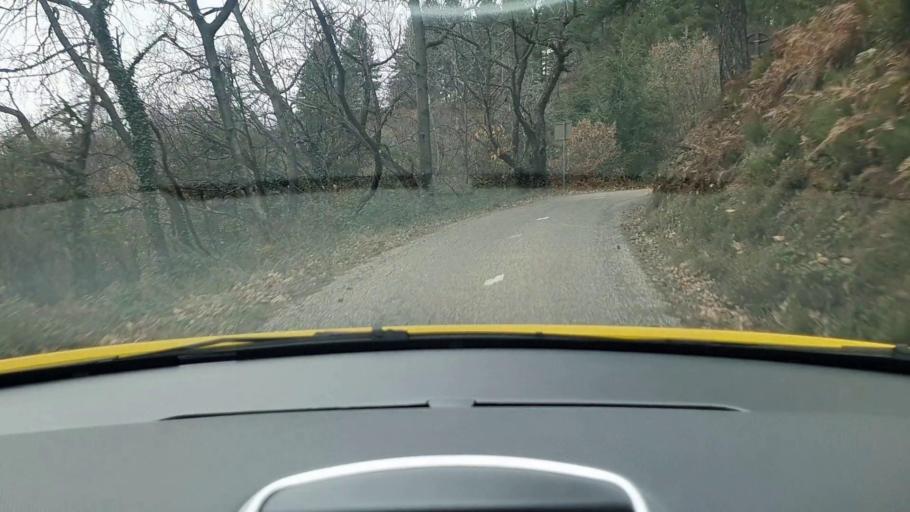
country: FR
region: Languedoc-Roussillon
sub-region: Departement du Gard
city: Besseges
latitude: 44.3558
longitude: 4.0213
